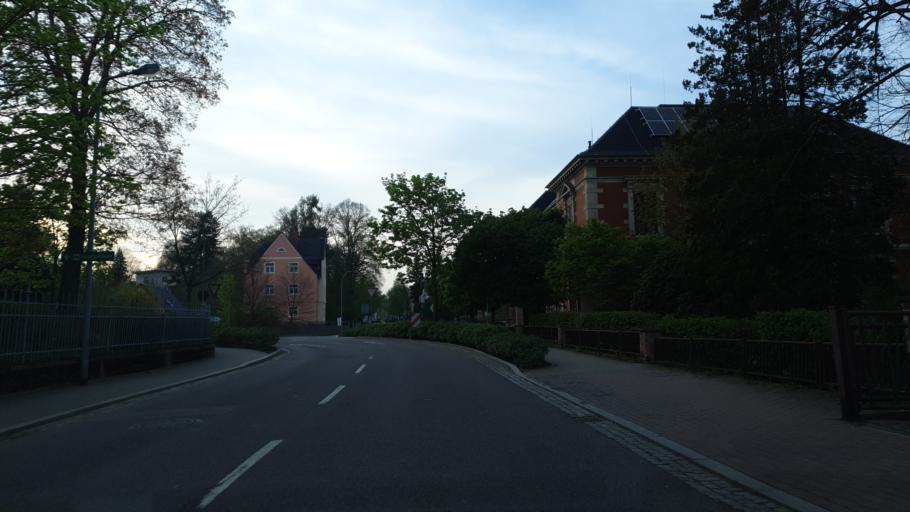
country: DE
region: Saxony
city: Lichtenstein
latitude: 50.7594
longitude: 12.6300
